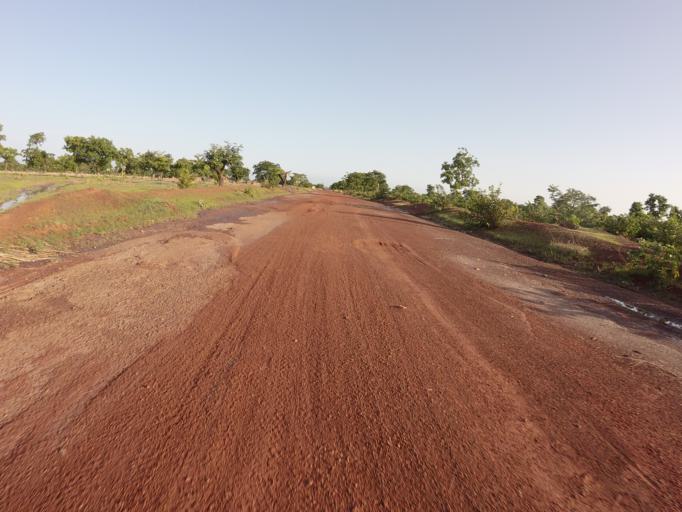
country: TG
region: Savanes
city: Sansanne-Mango
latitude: 10.3609
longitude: -0.0935
